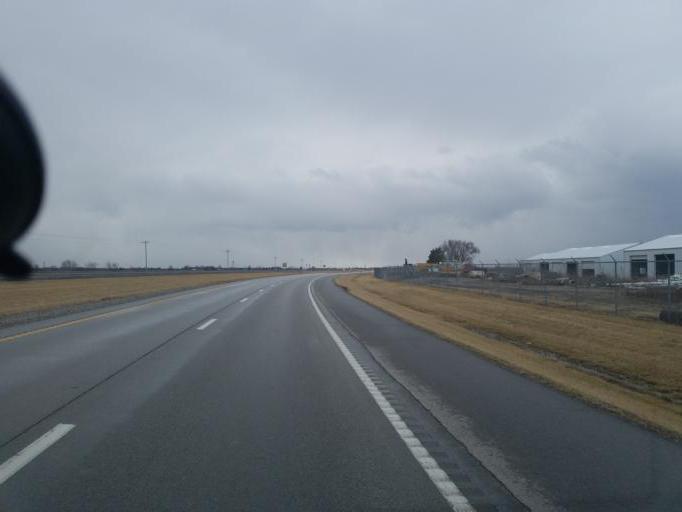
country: US
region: Missouri
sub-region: Macon County
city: Macon
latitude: 39.8190
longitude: -92.4727
